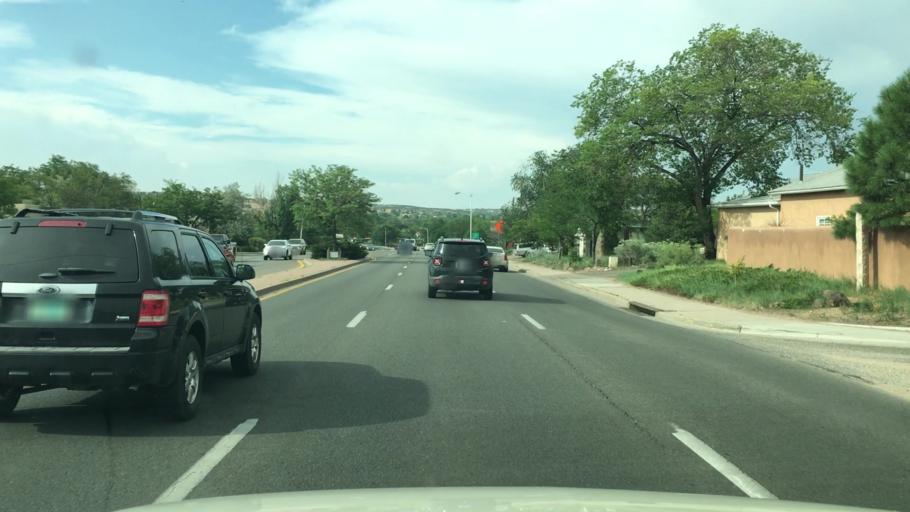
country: US
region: New Mexico
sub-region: Santa Fe County
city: Santa Fe
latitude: 35.6859
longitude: -105.9544
